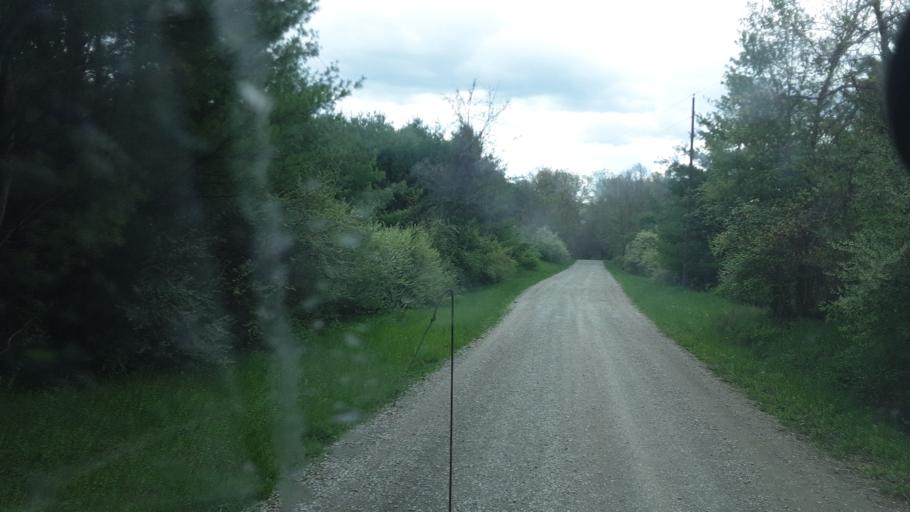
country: US
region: Ohio
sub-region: Noble County
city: Caldwell
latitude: 39.7503
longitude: -81.6190
